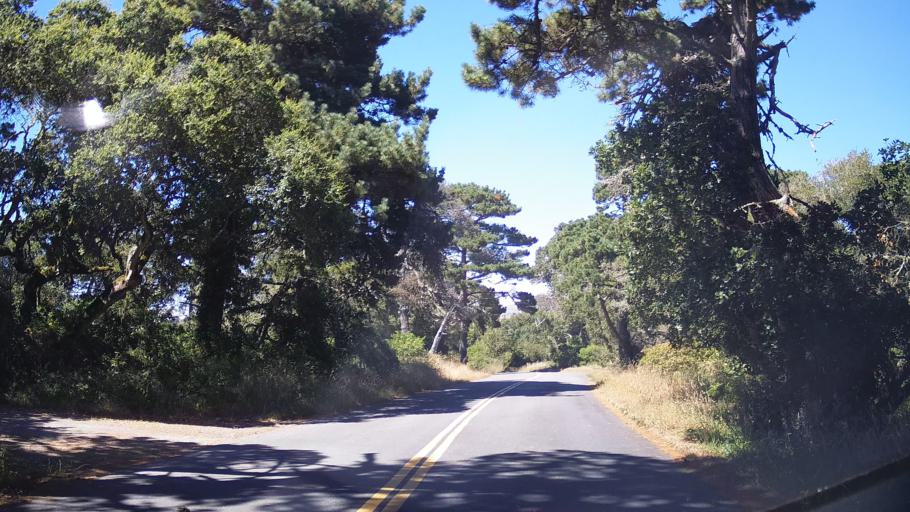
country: US
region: California
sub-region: Marin County
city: Inverness
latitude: 38.1320
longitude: -122.8970
